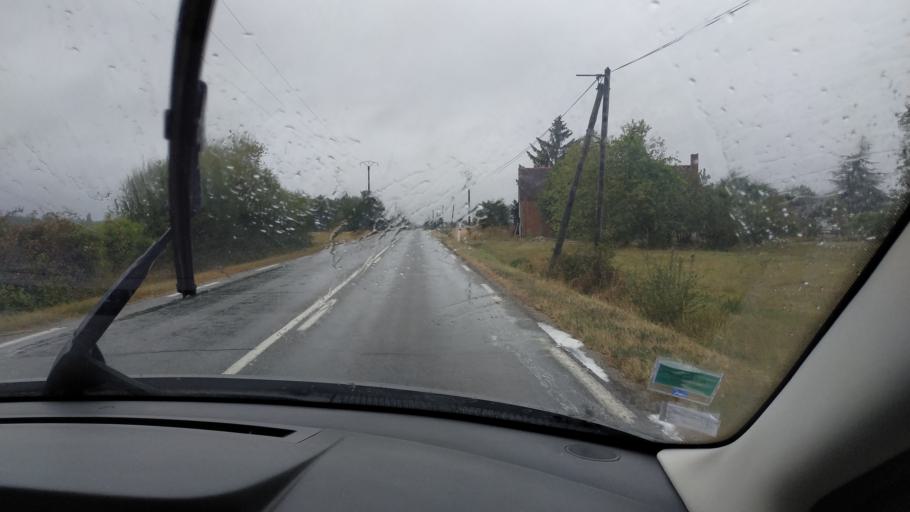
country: FR
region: Centre
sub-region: Departement du Loiret
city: Bellegarde
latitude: 47.9226
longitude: 2.3957
